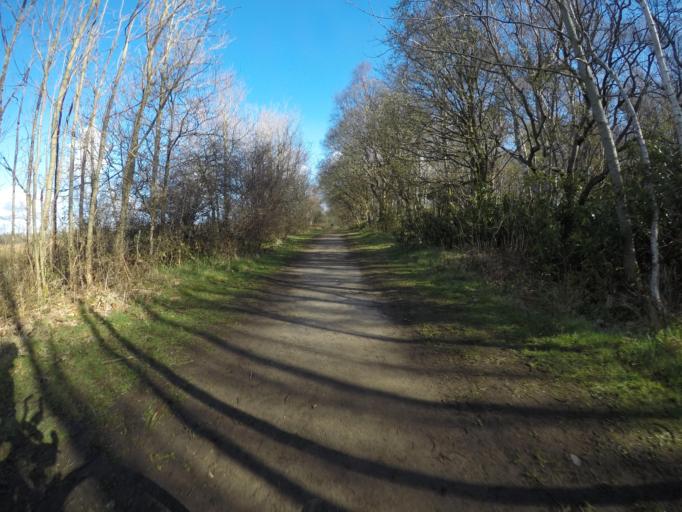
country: GB
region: Scotland
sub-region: North Ayrshire
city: Irvine
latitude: 55.6410
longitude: -4.6582
